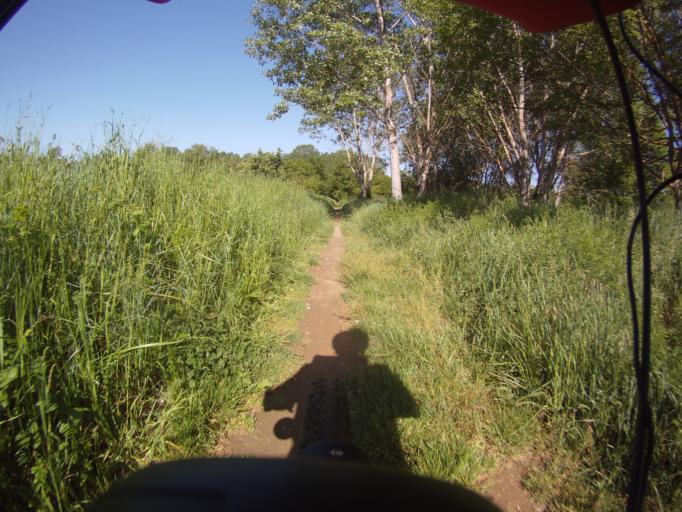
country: FR
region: Auvergne
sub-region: Departement du Puy-de-Dome
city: Mezel
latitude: 45.7561
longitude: 3.2219
